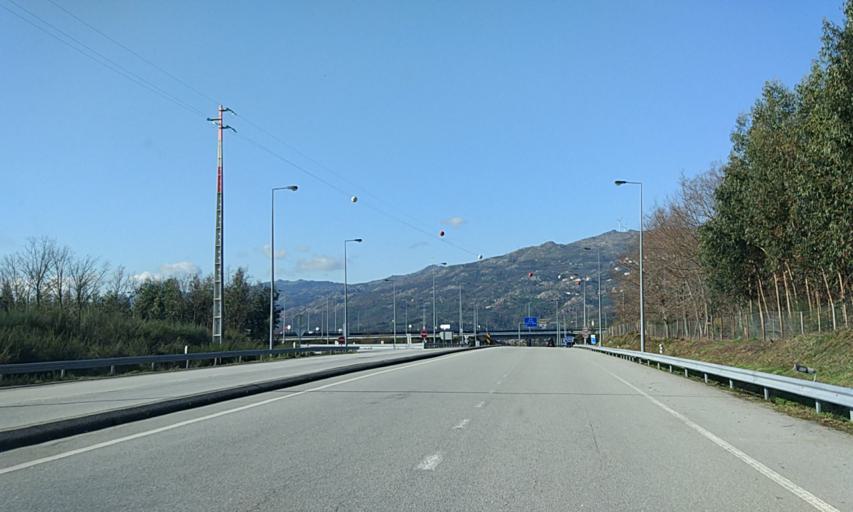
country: PT
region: Viseu
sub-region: Vouzela
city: Vouzela
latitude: 40.6483
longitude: -8.0574
